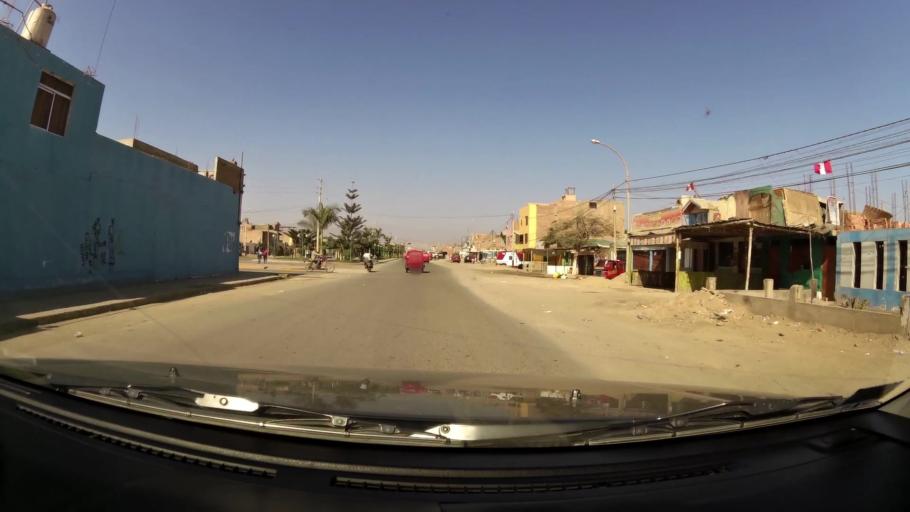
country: PE
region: Ica
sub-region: Provincia de Chincha
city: Chincha Alta
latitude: -13.4103
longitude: -76.1286
